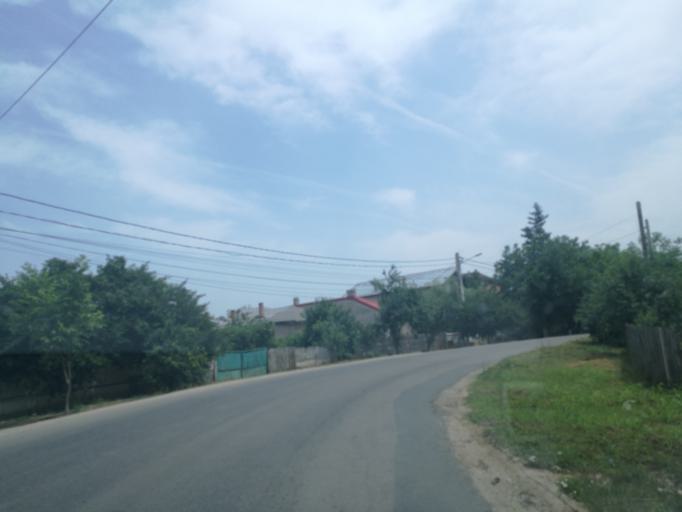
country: RO
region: Ilfov
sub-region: Comuna Vidra
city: Cretesti
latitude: 44.2722
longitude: 26.1477
